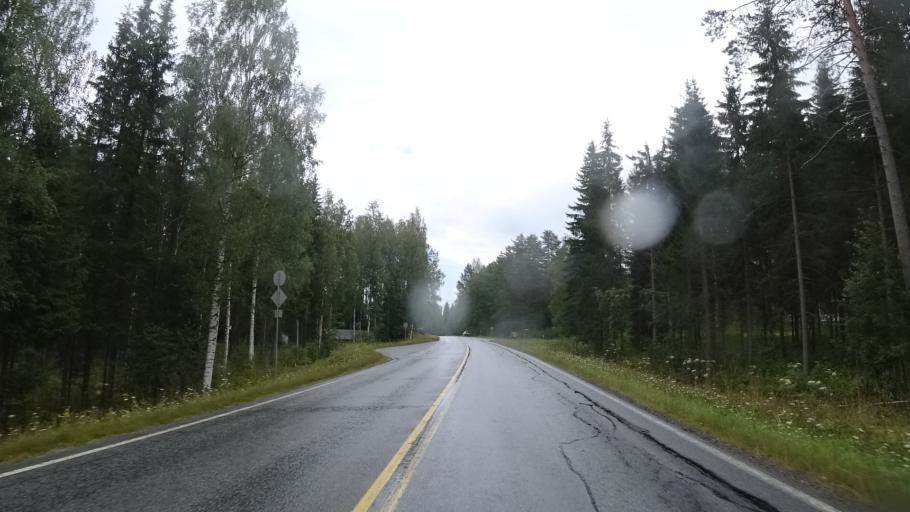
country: FI
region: North Karelia
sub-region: Keski-Karjala
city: Raeaekkylae
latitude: 62.0772
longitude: 29.6486
